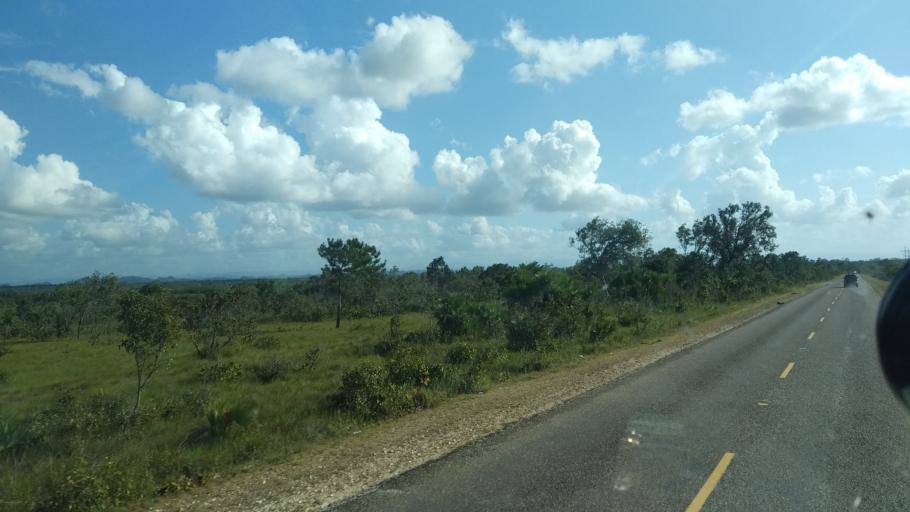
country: BZ
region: Cayo
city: Belmopan
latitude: 17.3869
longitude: -88.5164
